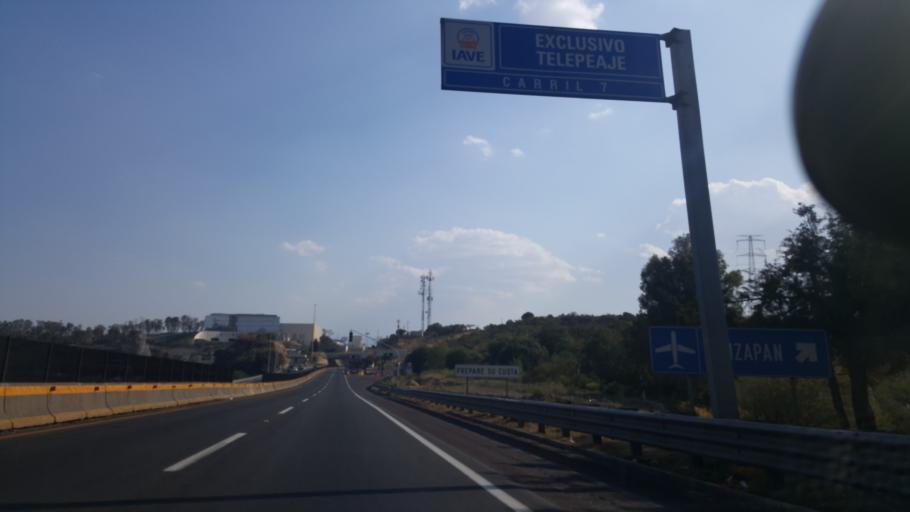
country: MX
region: Mexico
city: Ciudad Lopez Mateos
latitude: 19.5511
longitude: -99.2774
